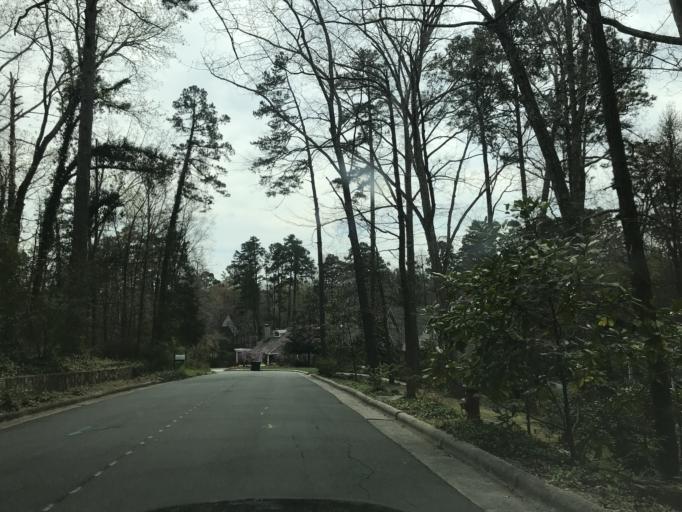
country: US
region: North Carolina
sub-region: Orange County
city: Chapel Hill
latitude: 35.9029
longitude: -79.0356
